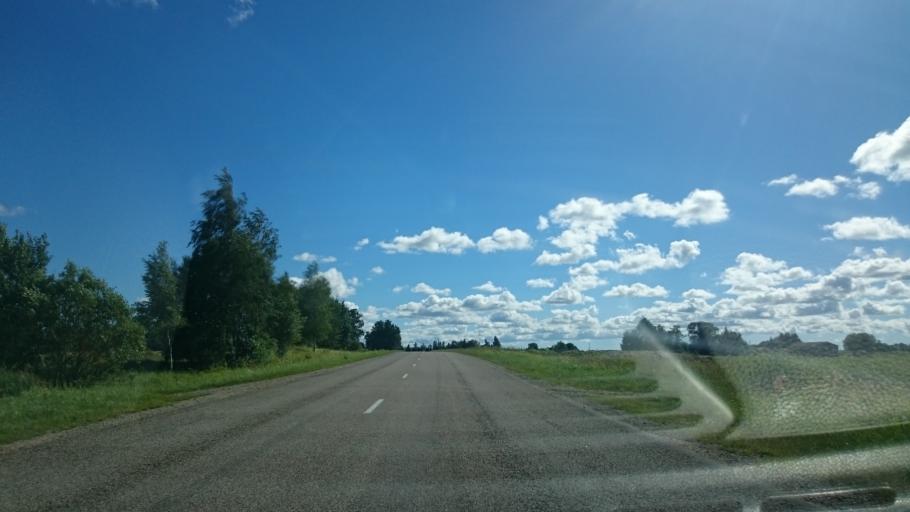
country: LV
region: Aizpute
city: Aizpute
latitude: 56.7672
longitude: 21.6222
